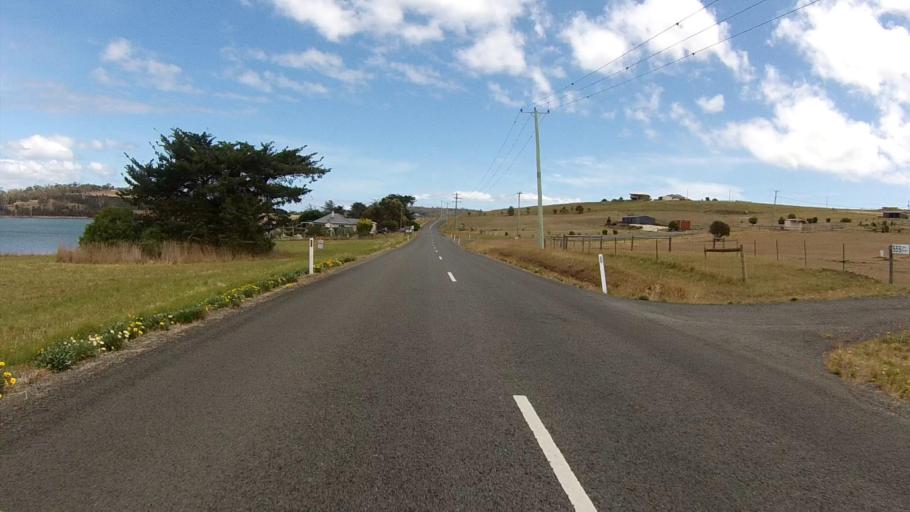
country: AU
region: Tasmania
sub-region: Sorell
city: Sorell
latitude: -42.8669
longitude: 147.6754
